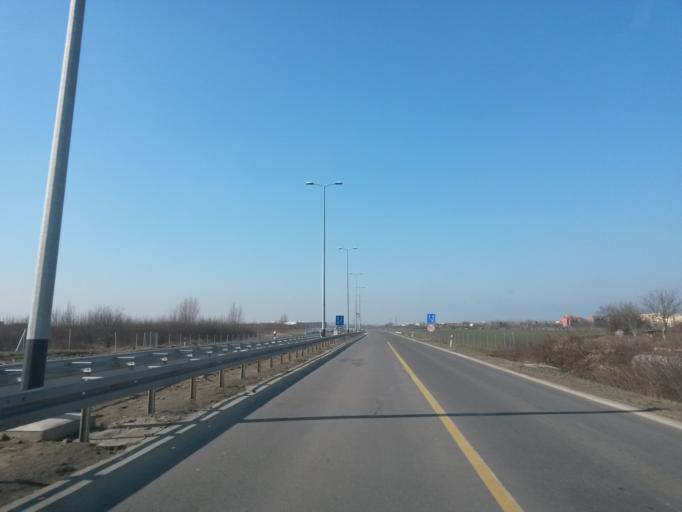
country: HR
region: Osjecko-Baranjska
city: Brijest
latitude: 45.5490
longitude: 18.6579
